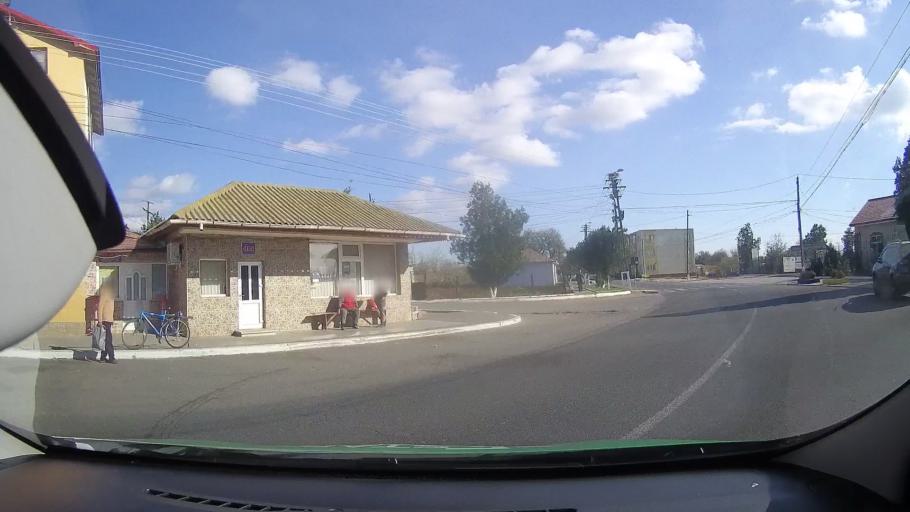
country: RO
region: Tulcea
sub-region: Comuna Ceamurlia de Jos
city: Ceamurlia de Jos
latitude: 44.7423
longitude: 28.7247
